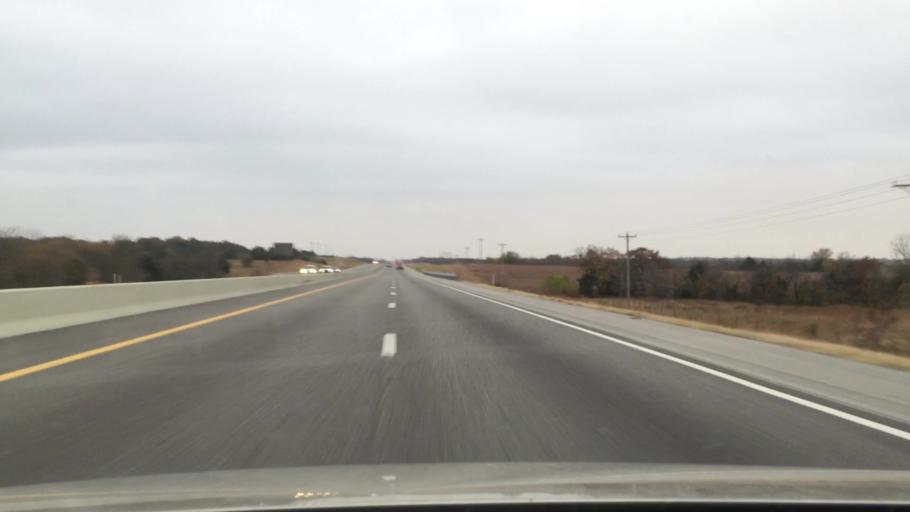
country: US
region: Oklahoma
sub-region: Lincoln County
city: Chandler
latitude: 35.7364
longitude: -96.7887
